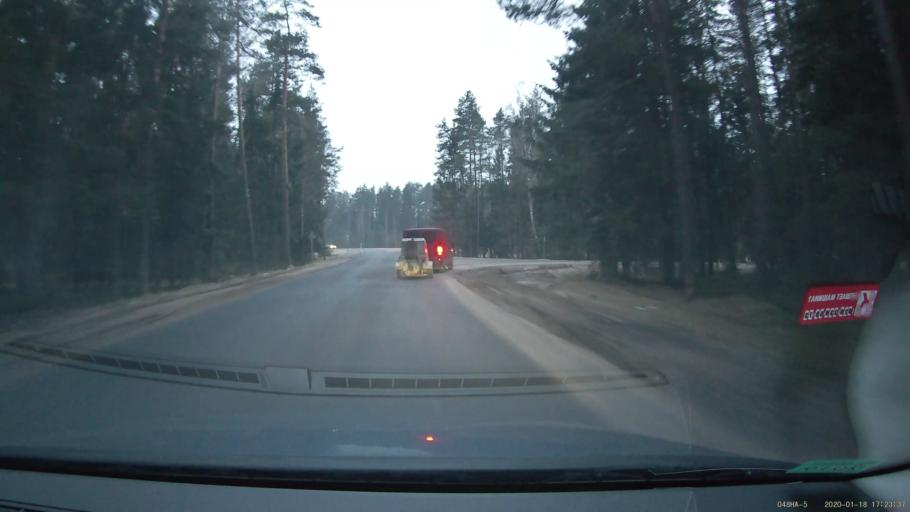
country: BY
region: Minsk
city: Rakaw
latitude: 53.9560
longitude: 27.1156
